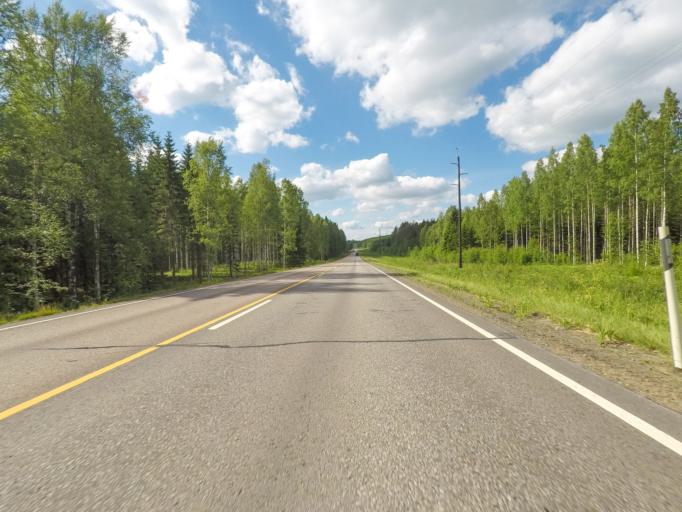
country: FI
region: Southern Savonia
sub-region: Savonlinna
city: Kerimaeki
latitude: 61.8545
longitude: 29.1657
